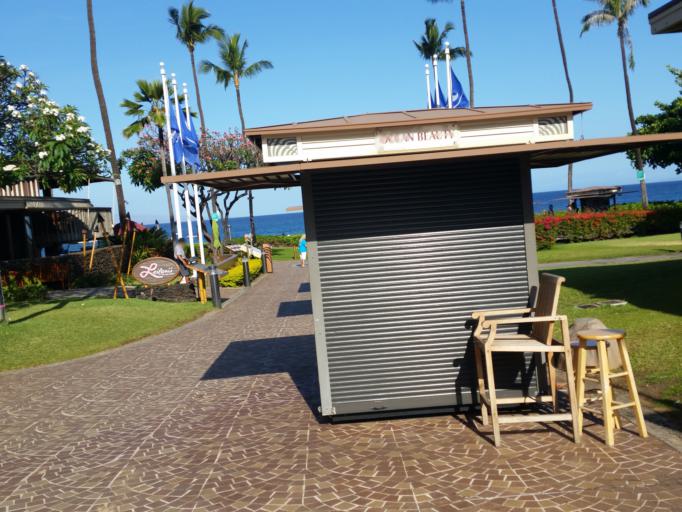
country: US
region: Hawaii
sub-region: Maui County
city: Ka'anapali
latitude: 20.9214
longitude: -156.6953
